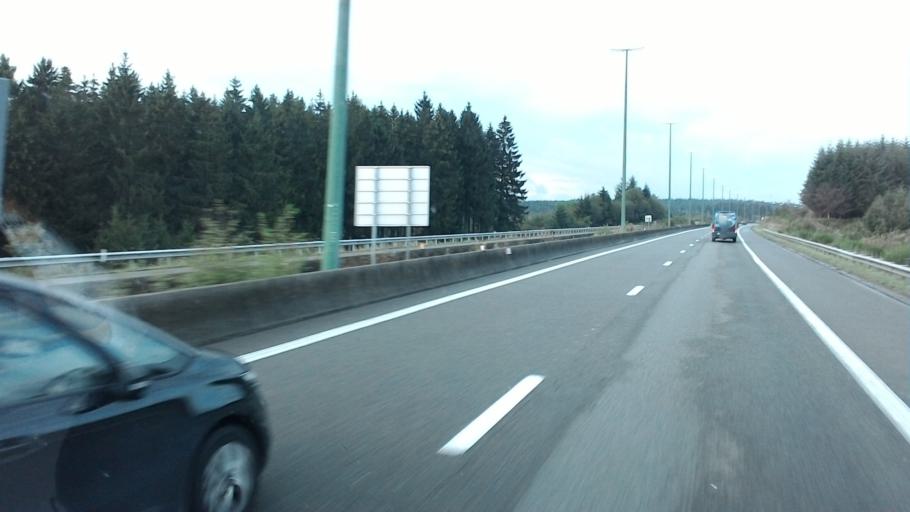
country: BE
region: Wallonia
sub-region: Province du Luxembourg
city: Bastogne
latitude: 50.0310
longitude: 5.7010
